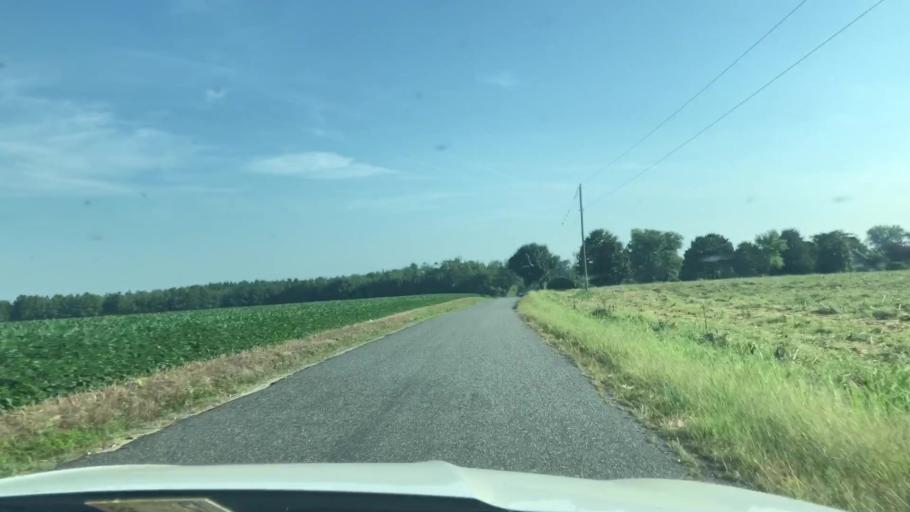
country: US
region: Virginia
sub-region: Middlesex County
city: Saluda
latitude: 37.6560
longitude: -76.6822
